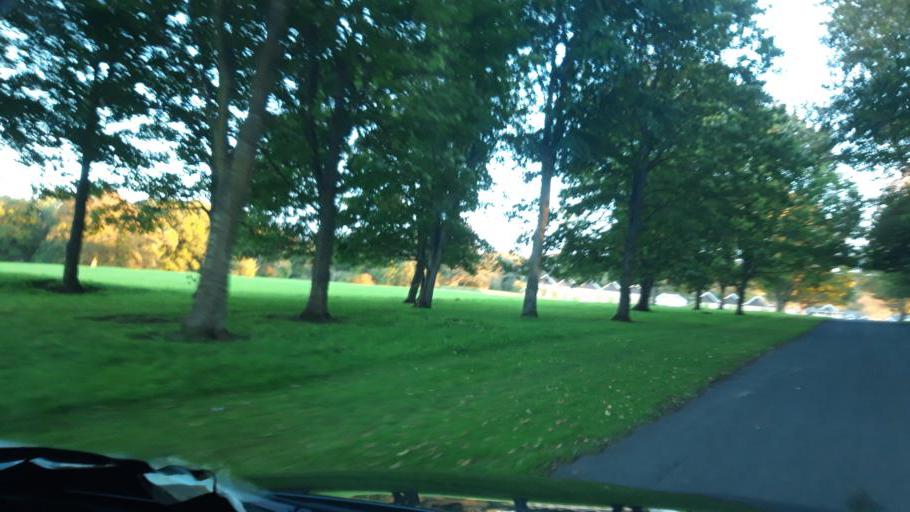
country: IE
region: Leinster
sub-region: Fingal County
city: Howth
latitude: 53.3829
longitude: -6.0775
